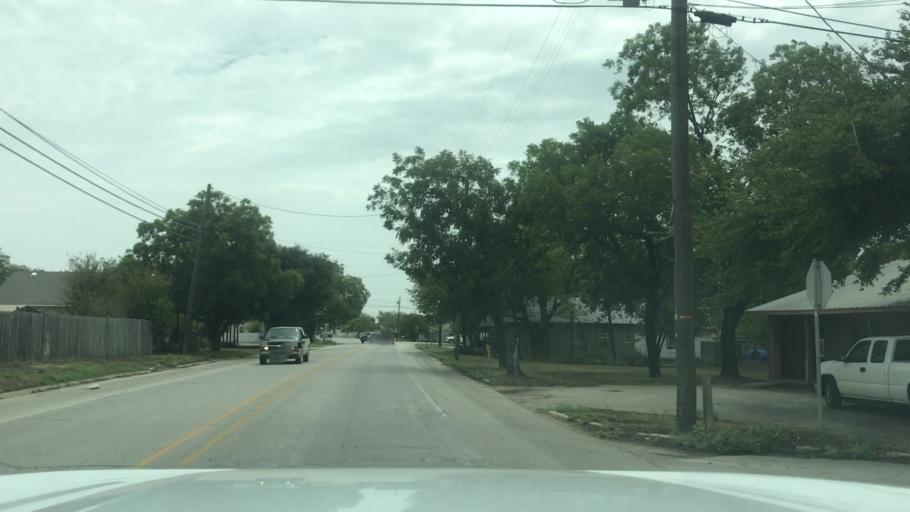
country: US
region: Texas
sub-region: Erath County
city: Dublin
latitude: 32.0836
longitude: -98.3360
